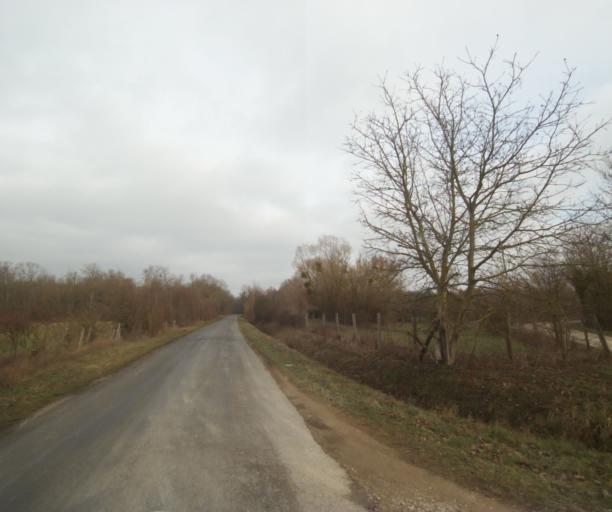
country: FR
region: Champagne-Ardenne
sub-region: Departement de la Haute-Marne
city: Villiers-en-Lieu
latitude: 48.6626
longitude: 4.8316
